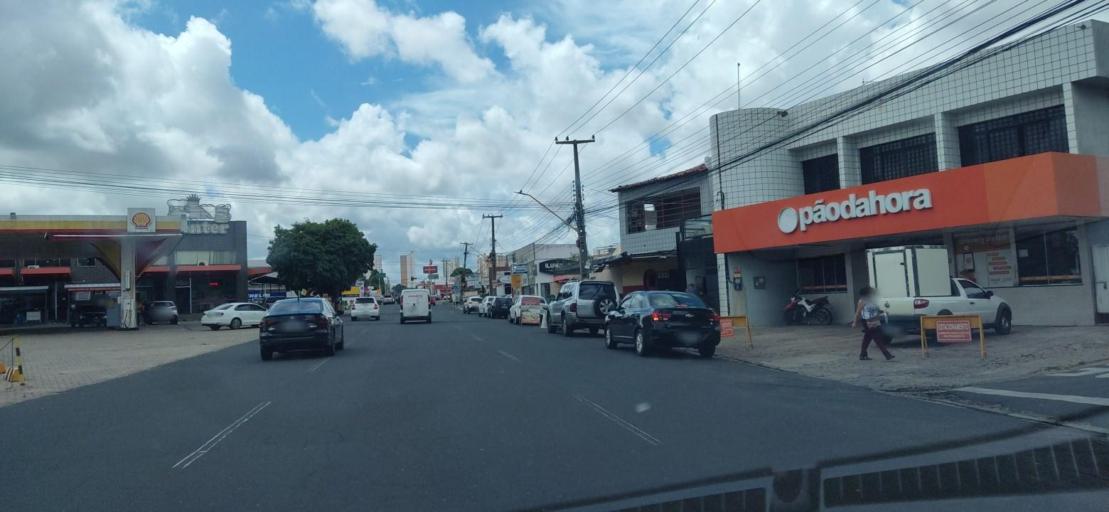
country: BR
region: Piaui
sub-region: Teresina
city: Teresina
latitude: -5.0630
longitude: -42.7962
